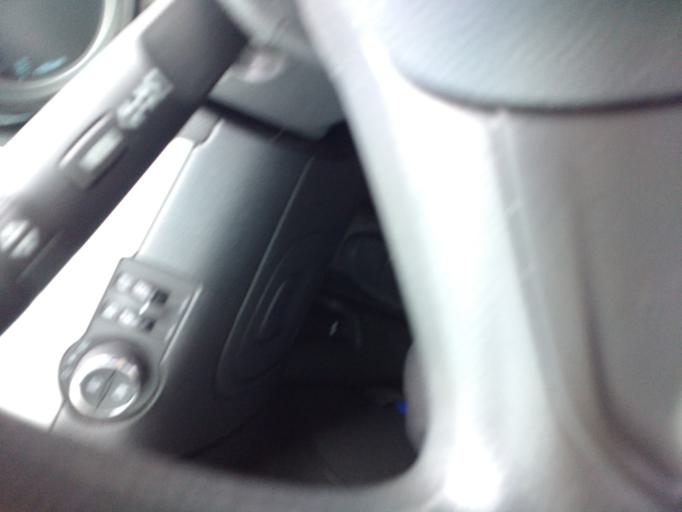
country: CN
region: Guangdong
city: Xinhui
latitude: 22.4601
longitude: 113.0330
